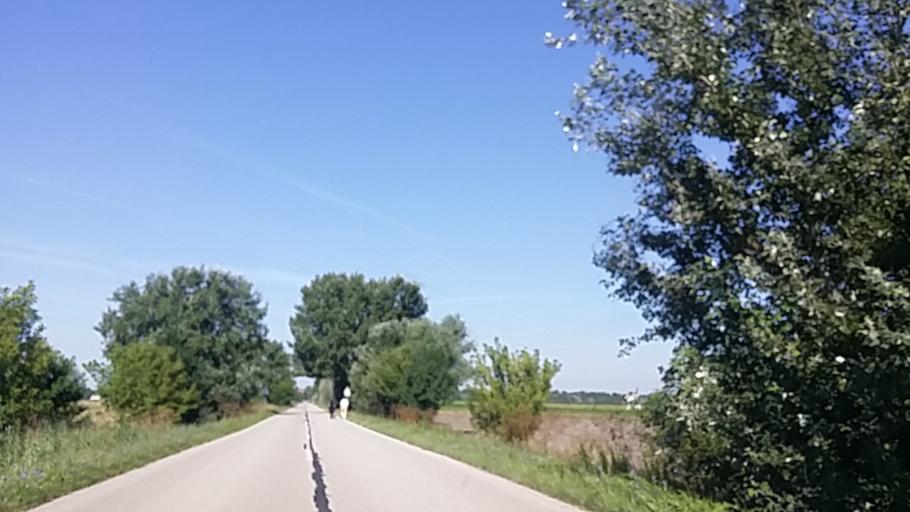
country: HU
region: Fejer
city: Adony
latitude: 47.1405
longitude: 18.8547
